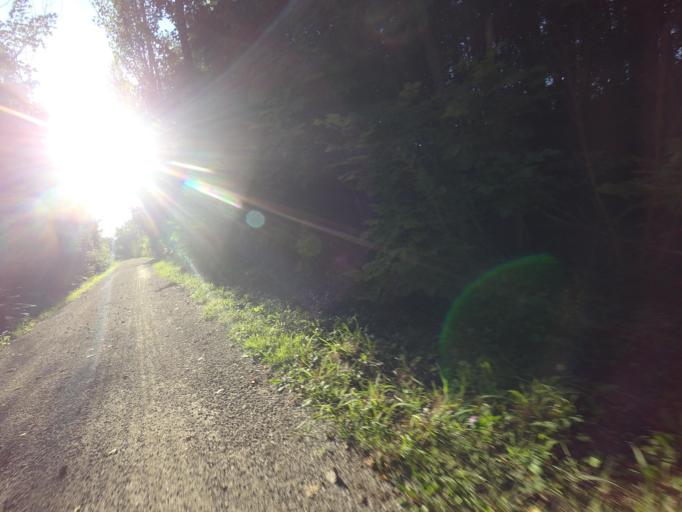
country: CA
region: Ontario
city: Goderich
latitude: 43.7605
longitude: -81.6963
